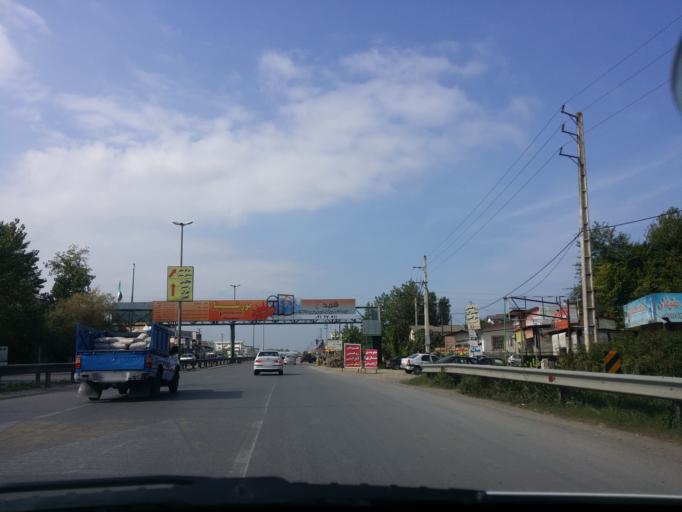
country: IR
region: Mazandaran
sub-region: Nowshahr
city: Nowshahr
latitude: 36.6378
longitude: 51.4904
